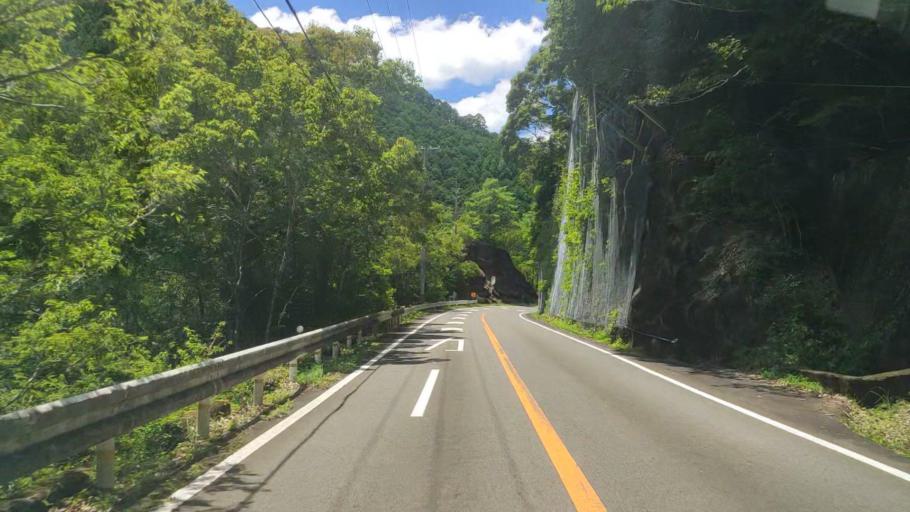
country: JP
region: Mie
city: Owase
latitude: 33.9976
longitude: 136.0191
